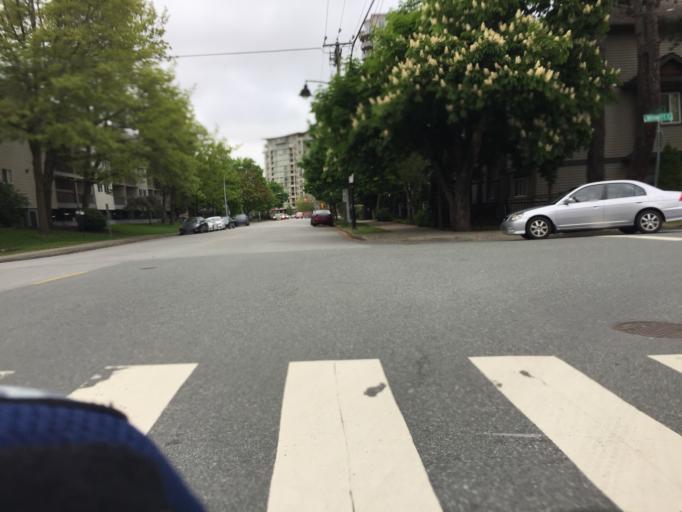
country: CA
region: British Columbia
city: Richmond
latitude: 49.1607
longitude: -123.1309
